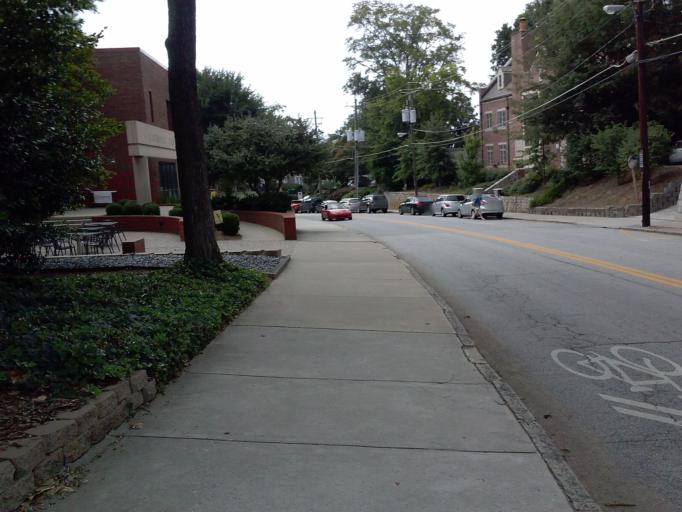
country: US
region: Georgia
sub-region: Fulton County
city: Atlanta
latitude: 33.7756
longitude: -84.3926
